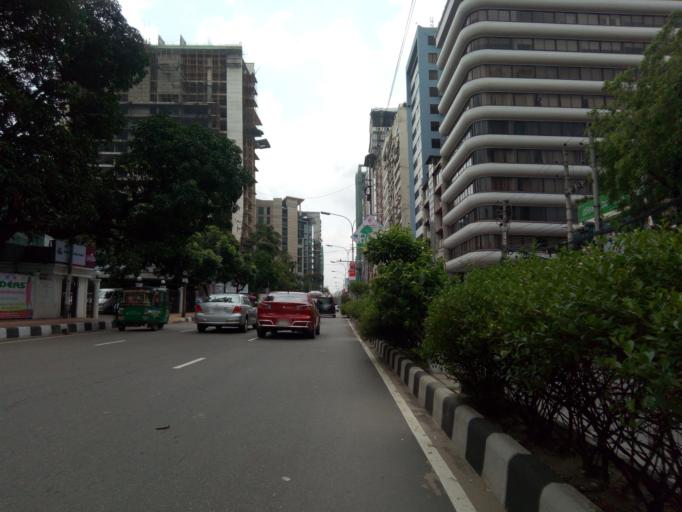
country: BD
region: Dhaka
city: Paltan
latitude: 23.7942
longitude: 90.4026
